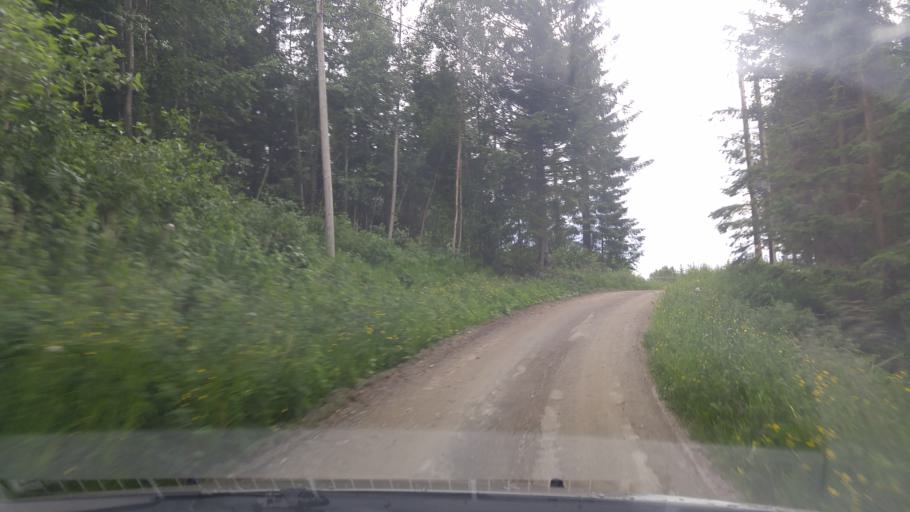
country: NO
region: Nord-Trondelag
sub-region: Levanger
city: Skogn
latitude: 63.6292
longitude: 11.2666
